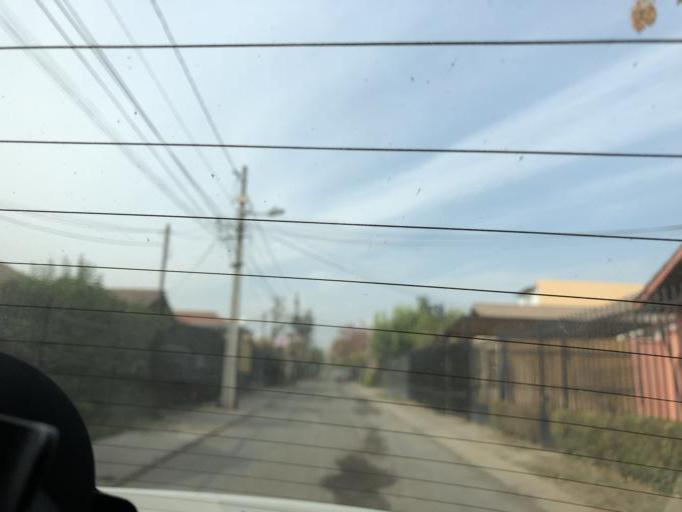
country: CL
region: Santiago Metropolitan
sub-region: Provincia de Cordillera
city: Puente Alto
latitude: -33.5498
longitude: -70.5600
